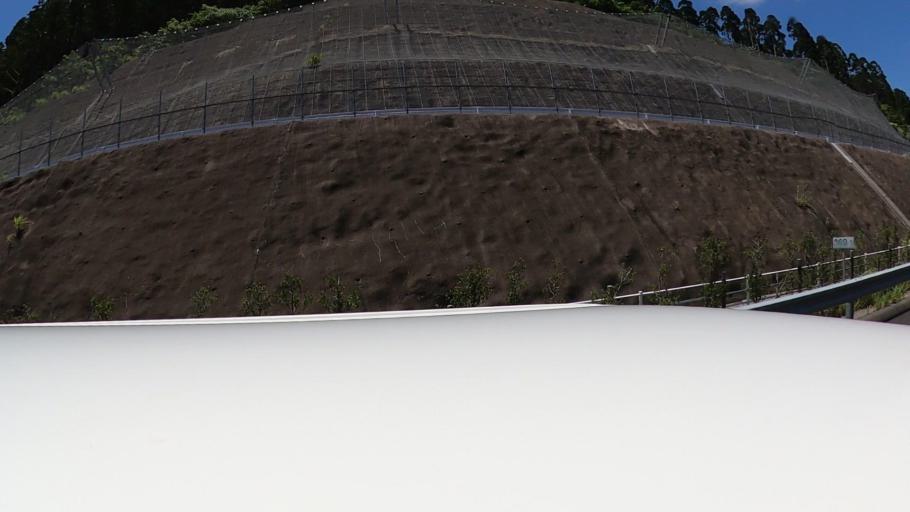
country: JP
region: Miyazaki
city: Nobeoka
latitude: 32.3923
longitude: 131.6219
